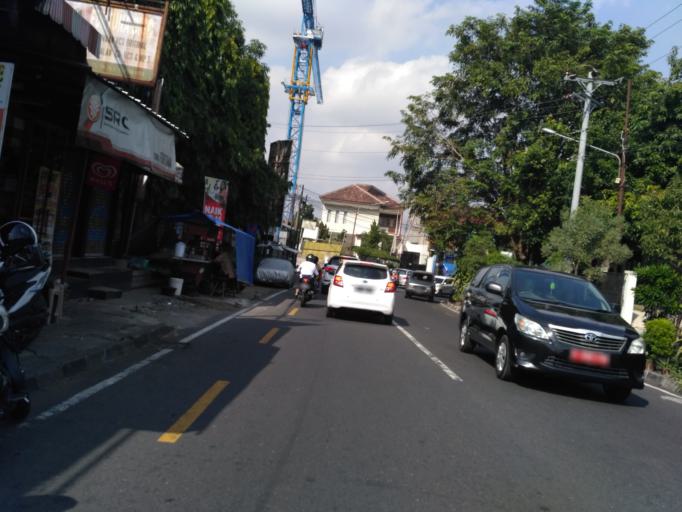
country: ID
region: Daerah Istimewa Yogyakarta
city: Yogyakarta
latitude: -7.7780
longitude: 110.3716
